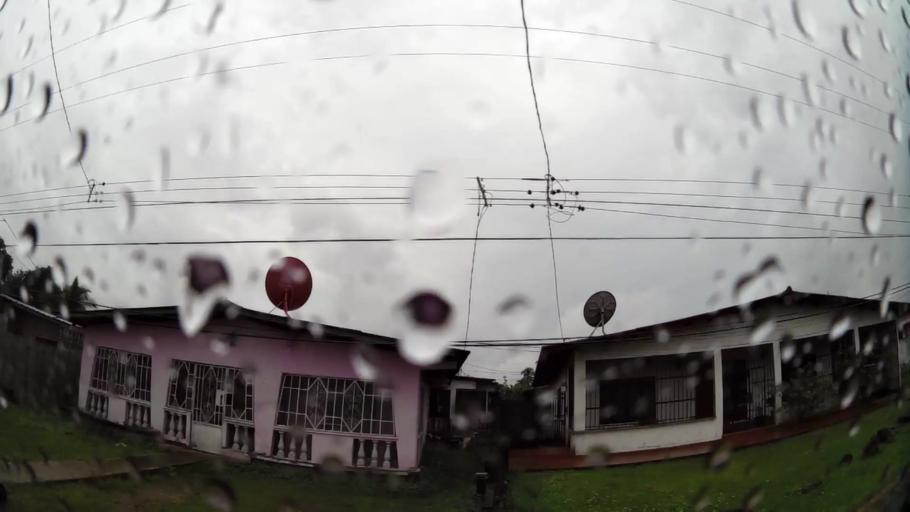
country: PA
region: Colon
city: Arco Iris
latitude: 9.3348
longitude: -79.8774
